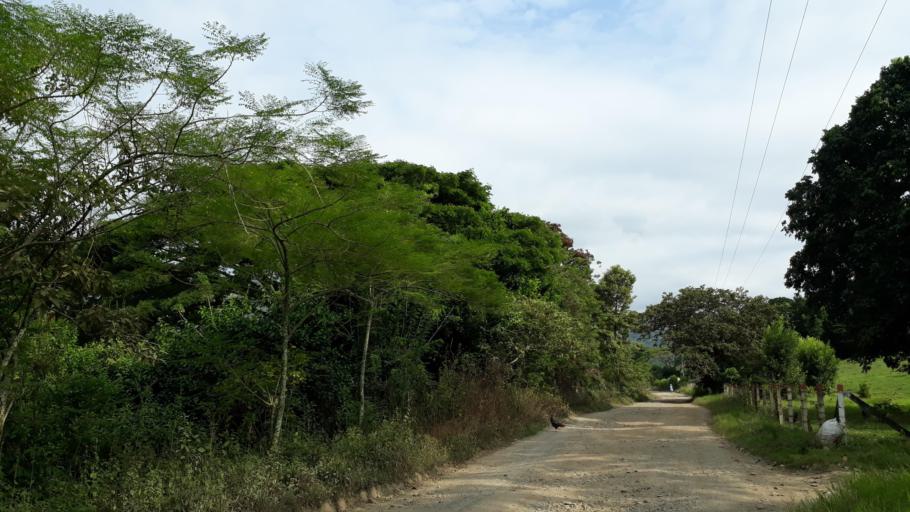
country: CO
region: Cauca
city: Buenos Aires
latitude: 3.1286
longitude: -76.6276
